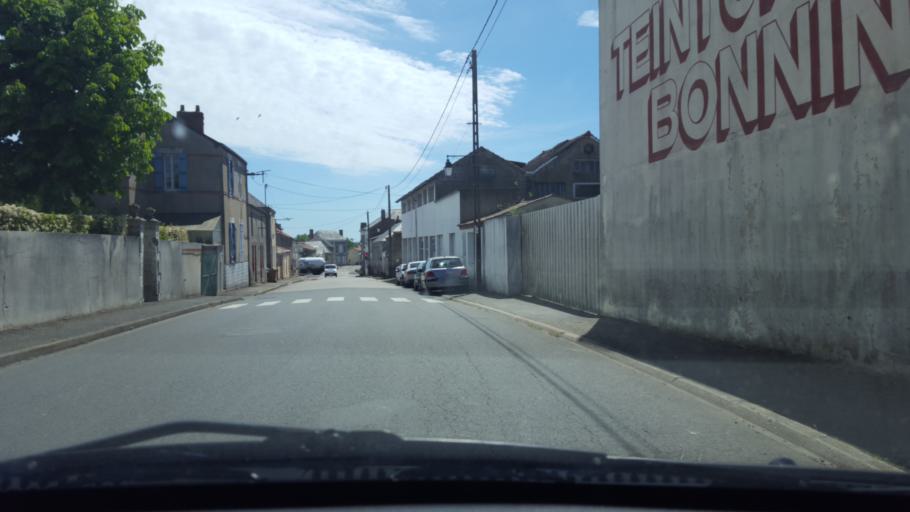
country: FR
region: Pays de la Loire
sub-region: Departement de la Loire-Atlantique
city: Touvois
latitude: 46.9038
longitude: -1.6845
